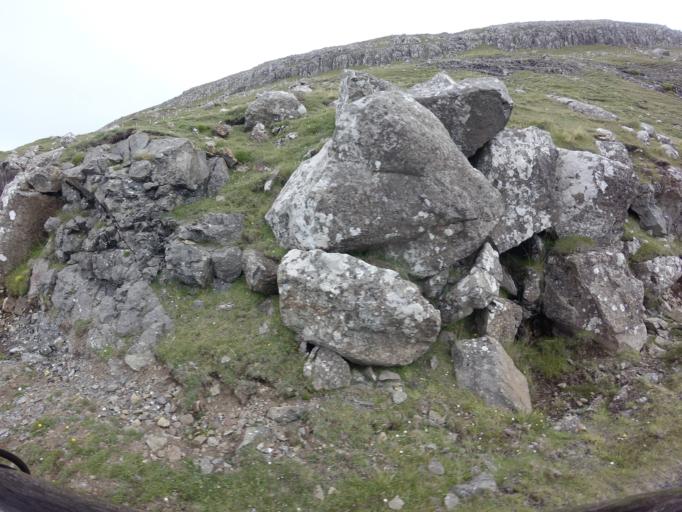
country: FO
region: Sandoy
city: Sandur
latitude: 61.8047
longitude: -6.7528
